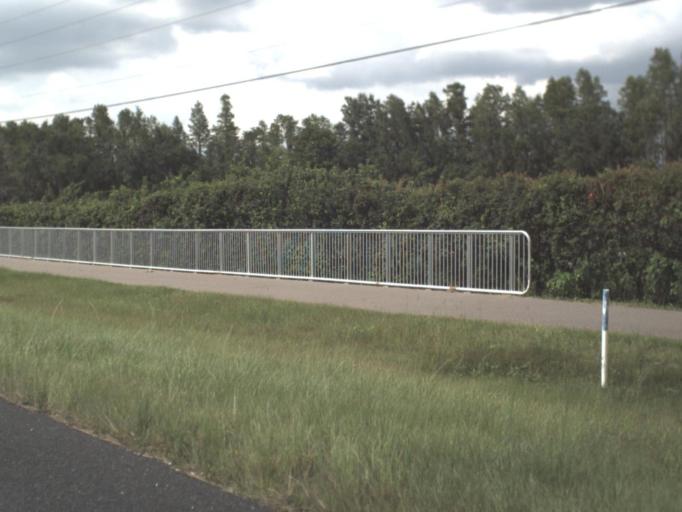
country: US
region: Florida
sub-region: Pasco County
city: Land O' Lakes
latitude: 28.2647
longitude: -82.4772
